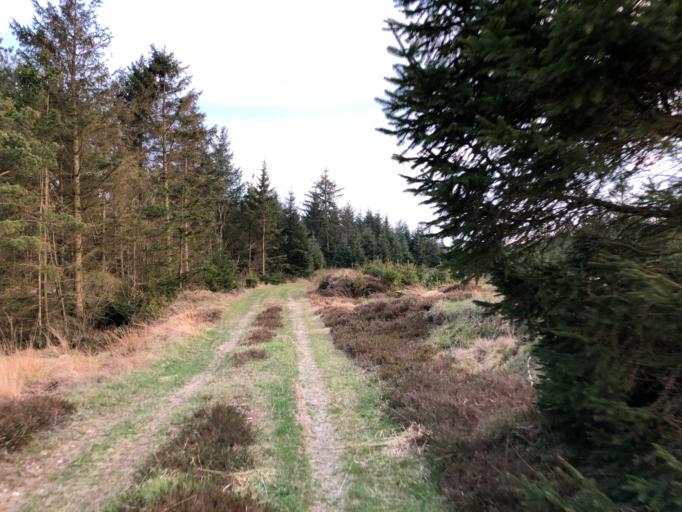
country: DK
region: Central Jutland
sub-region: Holstebro Kommune
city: Ulfborg
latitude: 56.2274
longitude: 8.4283
